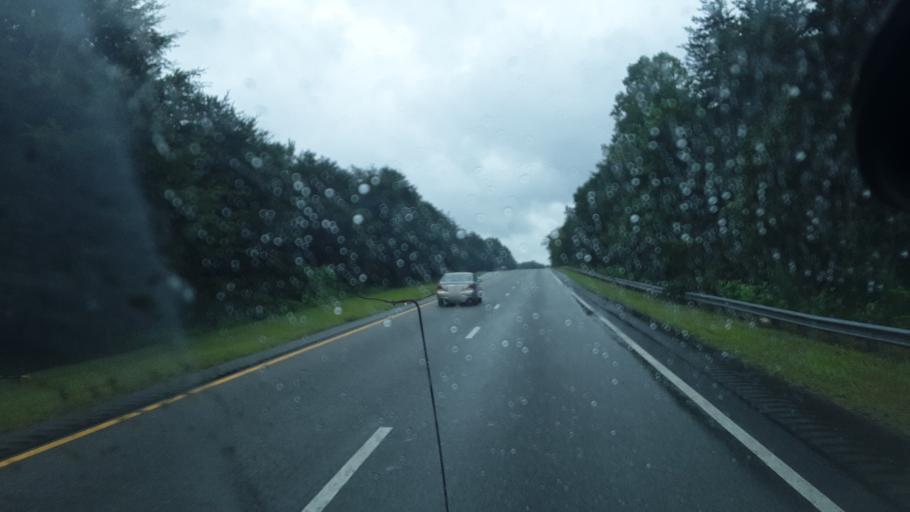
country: US
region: North Carolina
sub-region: Forsyth County
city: Winston-Salem
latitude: 36.0614
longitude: -80.1912
